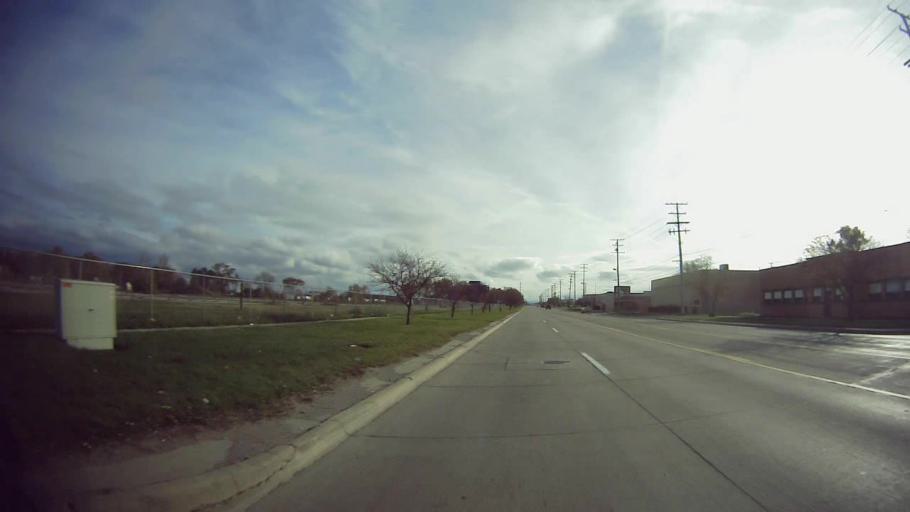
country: US
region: Michigan
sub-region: Macomb County
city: Warren
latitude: 42.4635
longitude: -83.0056
